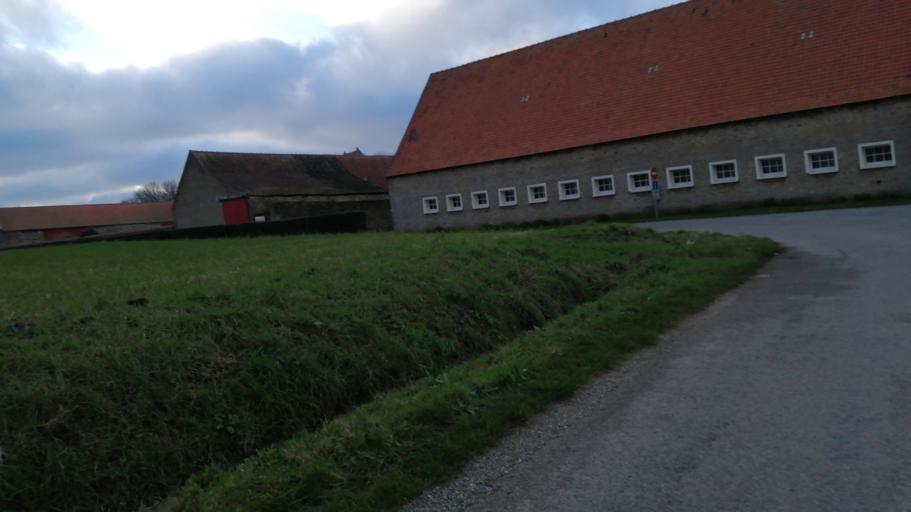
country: FR
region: Nord-Pas-de-Calais
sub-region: Departement du Pas-de-Calais
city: Ambleteuse
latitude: 50.8544
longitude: 1.5923
